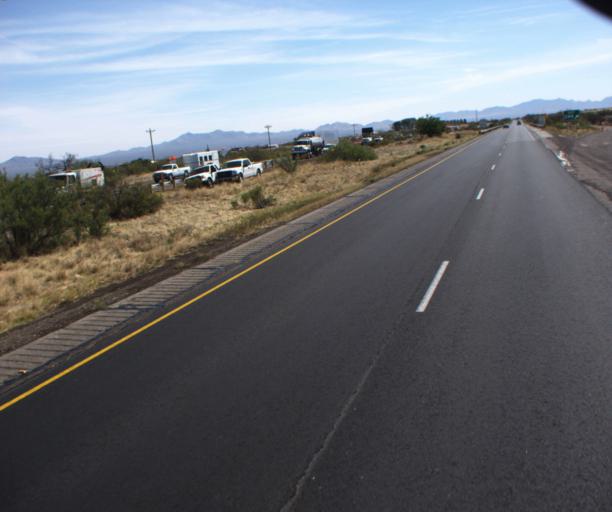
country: US
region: Arizona
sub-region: Cochise County
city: Mescal
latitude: 31.9629
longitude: -110.4003
